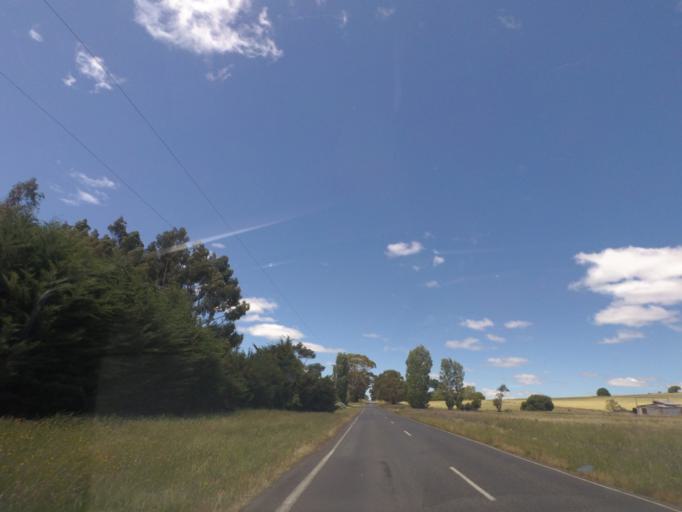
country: AU
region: Victoria
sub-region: Mount Alexander
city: Castlemaine
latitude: -37.3228
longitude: 144.1968
